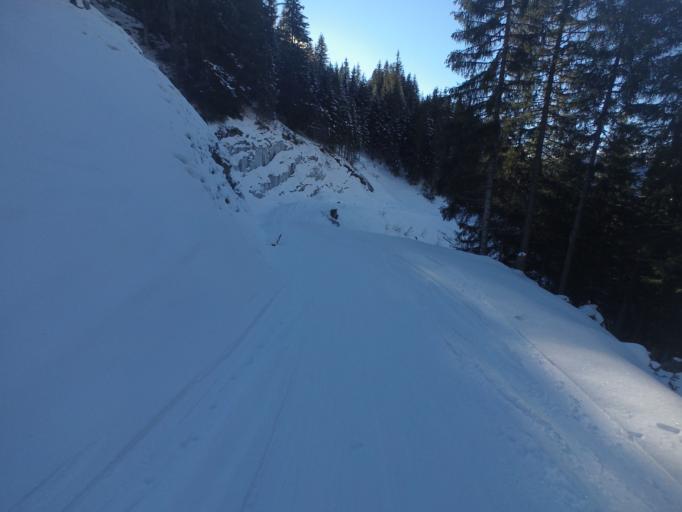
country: AT
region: Salzburg
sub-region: Politischer Bezirk Sankt Johann im Pongau
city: Huttschlag
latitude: 47.1826
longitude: 13.2786
